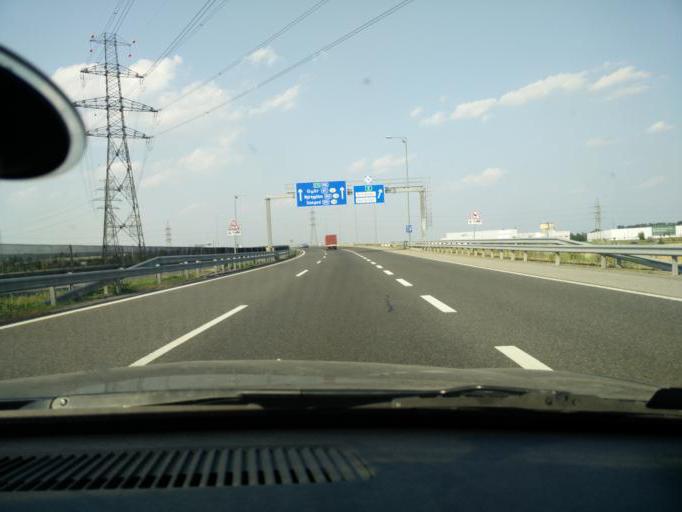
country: HU
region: Pest
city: Diosd
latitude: 47.3804
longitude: 18.9538
